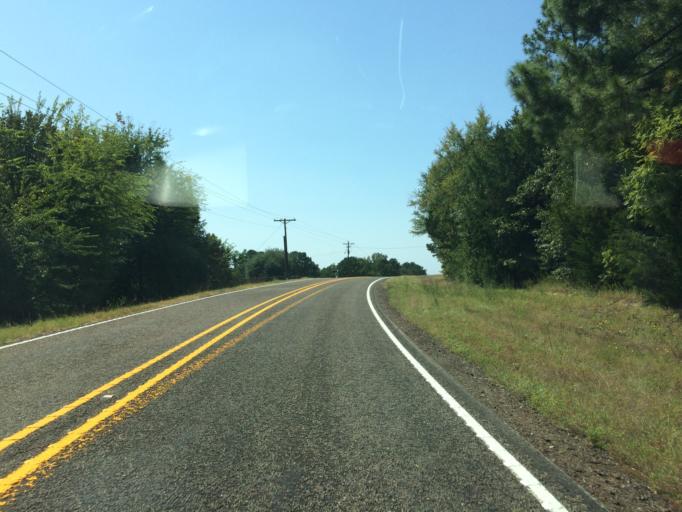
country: US
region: Texas
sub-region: Wood County
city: Quitman
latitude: 32.7291
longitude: -95.3270
